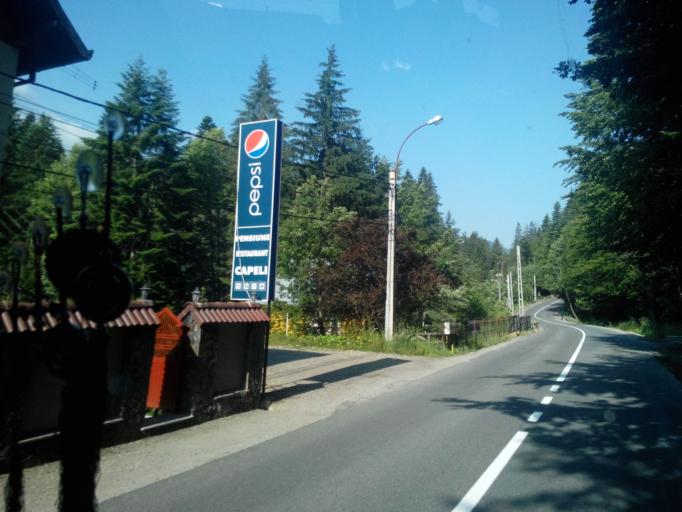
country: RO
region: Brasov
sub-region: Oras Predeal
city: Predeal
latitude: 45.4984
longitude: 25.5287
